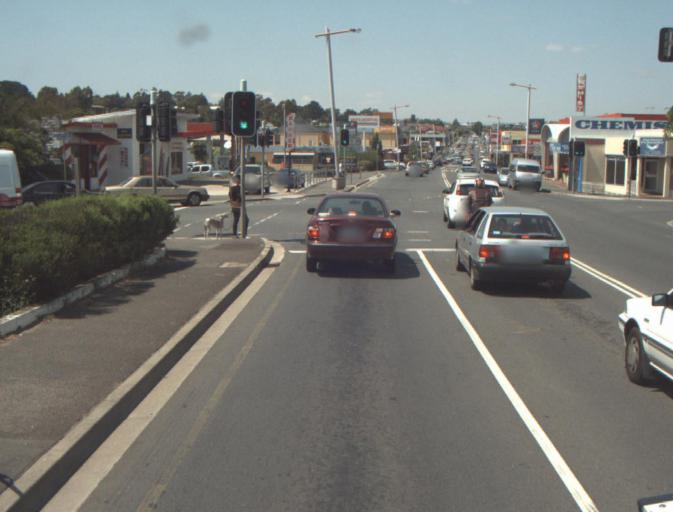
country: AU
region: Tasmania
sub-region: Launceston
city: East Launceston
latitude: -41.4645
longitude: 147.1587
